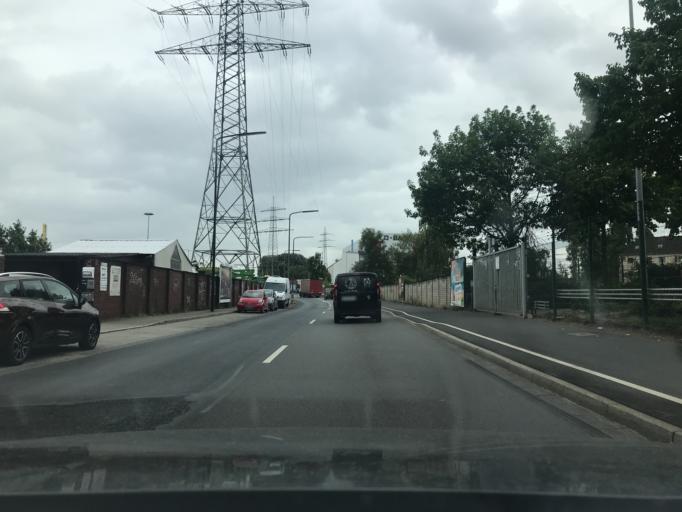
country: DE
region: North Rhine-Westphalia
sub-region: Regierungsbezirk Dusseldorf
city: Erkrath
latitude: 51.1868
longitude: 6.8524
